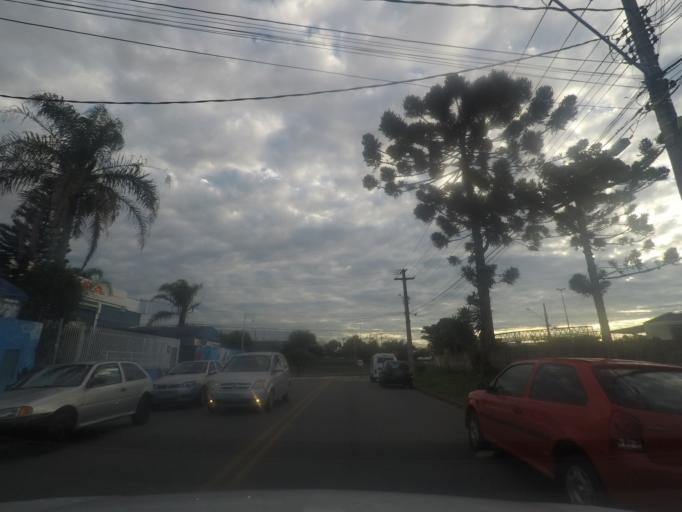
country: BR
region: Parana
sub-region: Pinhais
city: Pinhais
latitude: -25.4694
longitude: -49.2113
